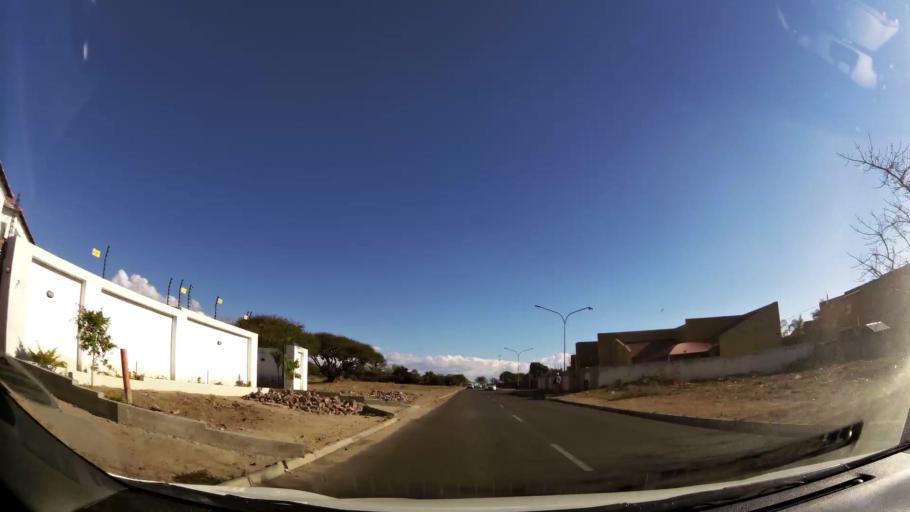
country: ZA
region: Limpopo
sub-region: Capricorn District Municipality
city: Polokwane
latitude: -23.8826
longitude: 29.4871
